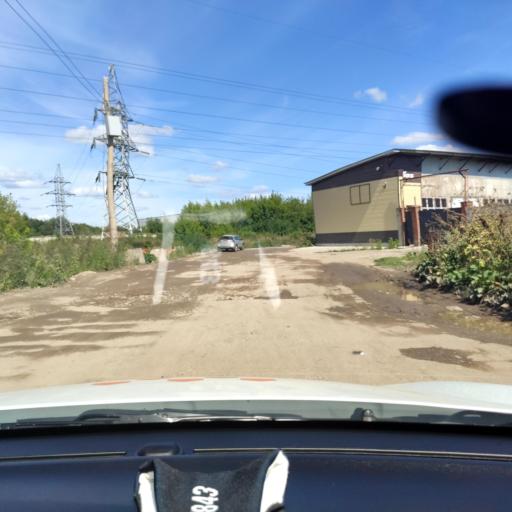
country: RU
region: Tatarstan
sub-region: Gorod Kazan'
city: Kazan
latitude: 55.8229
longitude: 49.2004
